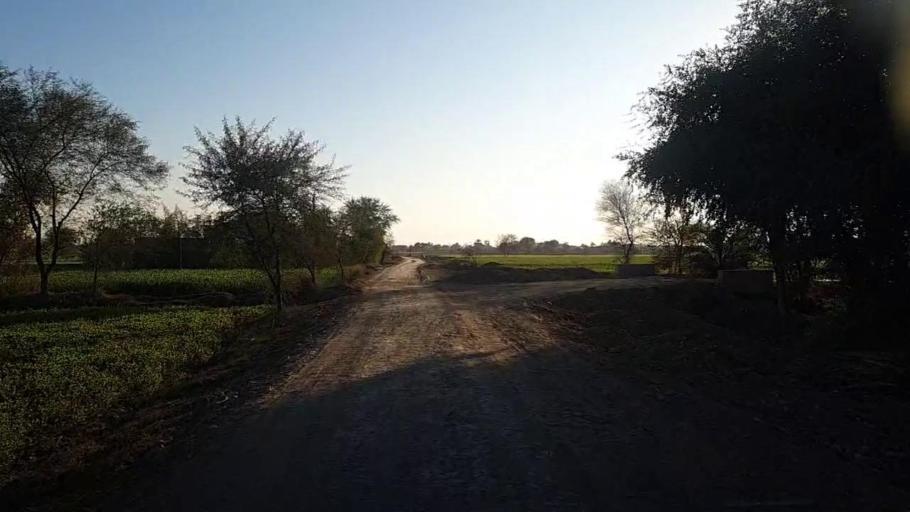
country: PK
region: Sindh
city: Khairpur
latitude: 27.8965
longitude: 69.7000
